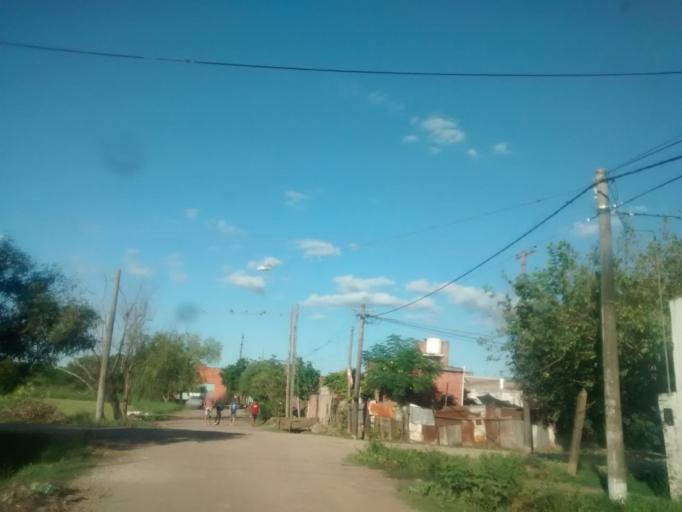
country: AR
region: Chaco
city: Resistencia
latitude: -27.4380
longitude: -58.9747
